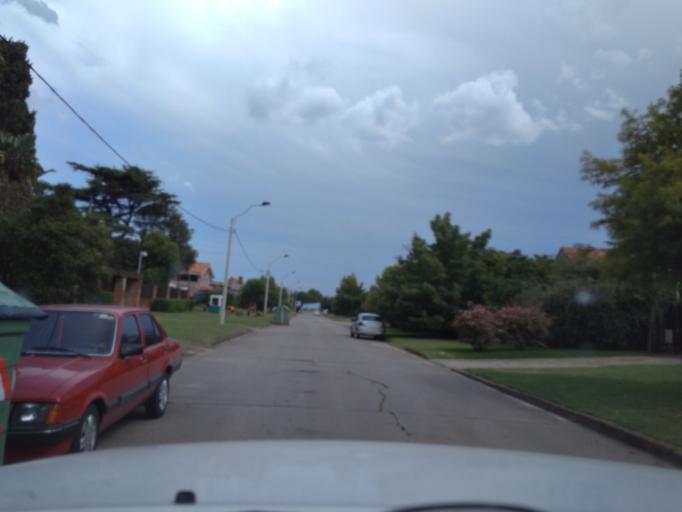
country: UY
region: Canelones
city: Barra de Carrasco
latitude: -34.8848
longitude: -56.0482
